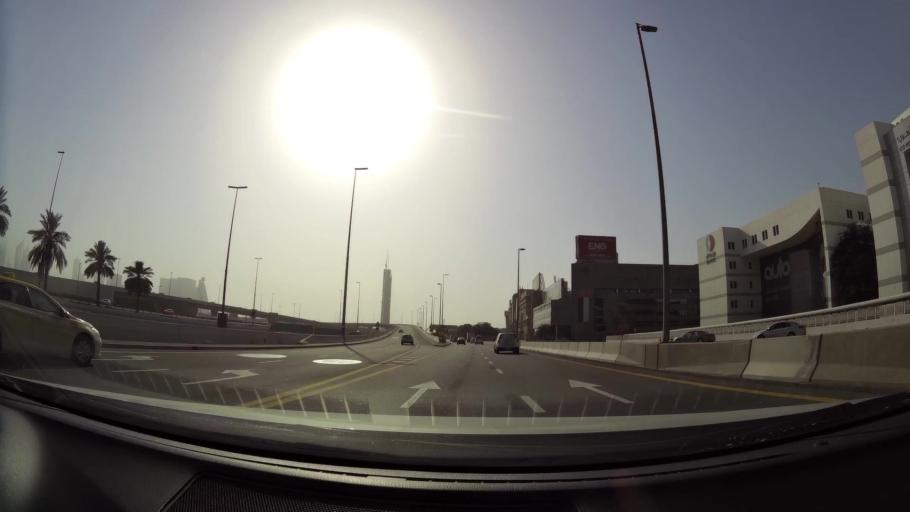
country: AE
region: Ash Shariqah
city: Sharjah
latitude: 25.2324
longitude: 55.3102
